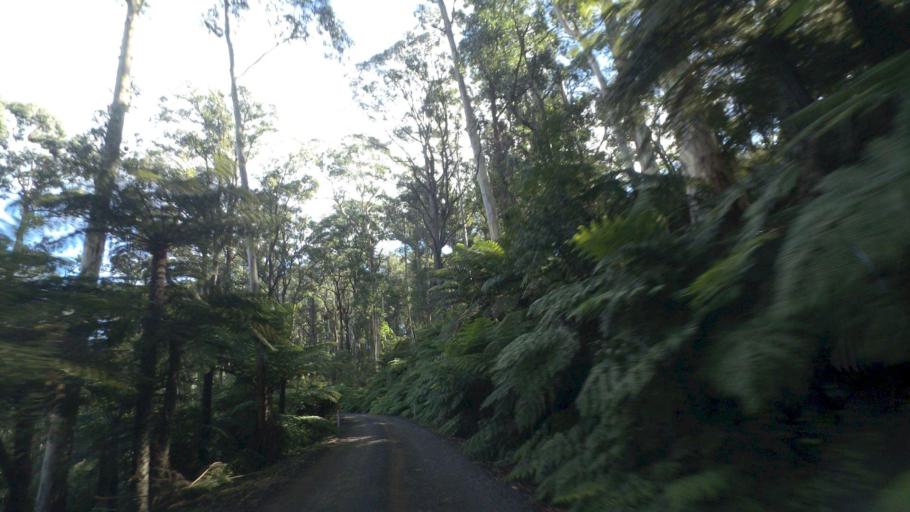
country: AU
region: Victoria
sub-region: Cardinia
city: Gembrook
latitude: -37.9310
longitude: 145.5914
